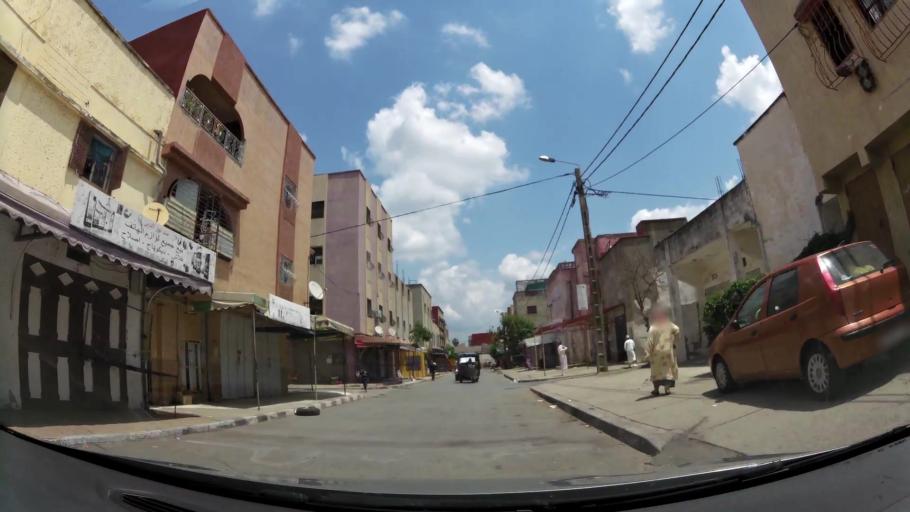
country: MA
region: Rabat-Sale-Zemmour-Zaer
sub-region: Khemisset
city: Tiflet
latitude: 34.0036
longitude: -6.5311
